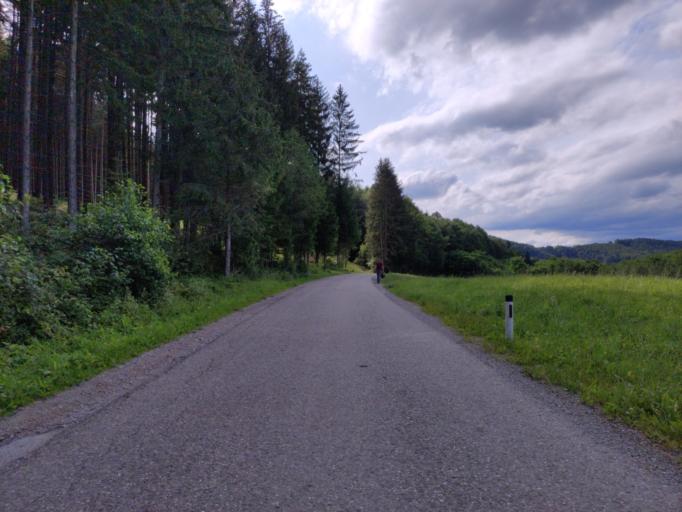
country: AT
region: Styria
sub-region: Politischer Bezirk Graz-Umgebung
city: Thal
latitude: 47.0636
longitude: 15.3439
